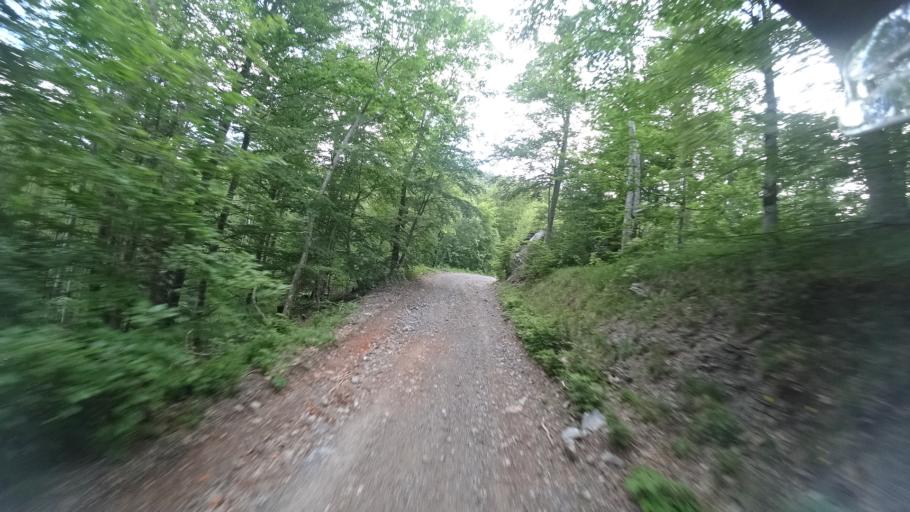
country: HR
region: Licko-Senjska
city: Gospic
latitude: 44.4413
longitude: 15.3004
